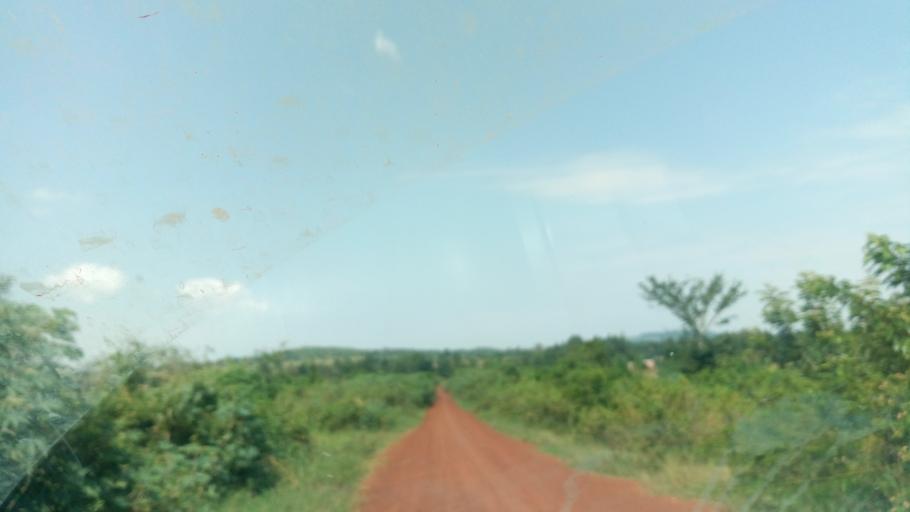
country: UG
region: Western Region
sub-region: Masindi District
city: Masindi
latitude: 1.6727
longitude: 31.8273
